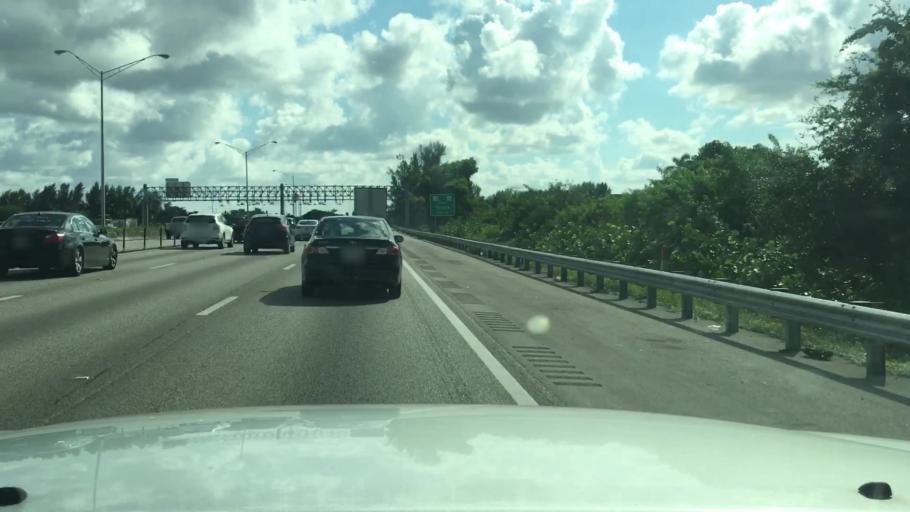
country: US
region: Florida
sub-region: Miami-Dade County
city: Ives Estates
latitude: 25.9499
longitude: -80.1828
